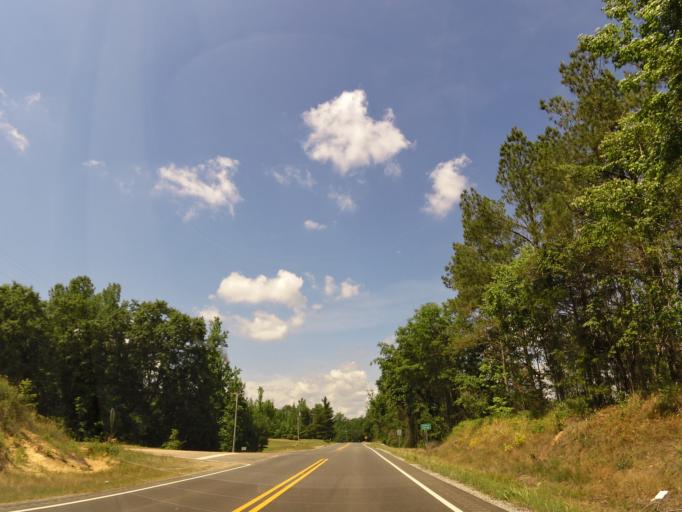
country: US
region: Alabama
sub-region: Marion County
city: Guin
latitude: 33.9378
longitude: -88.0034
